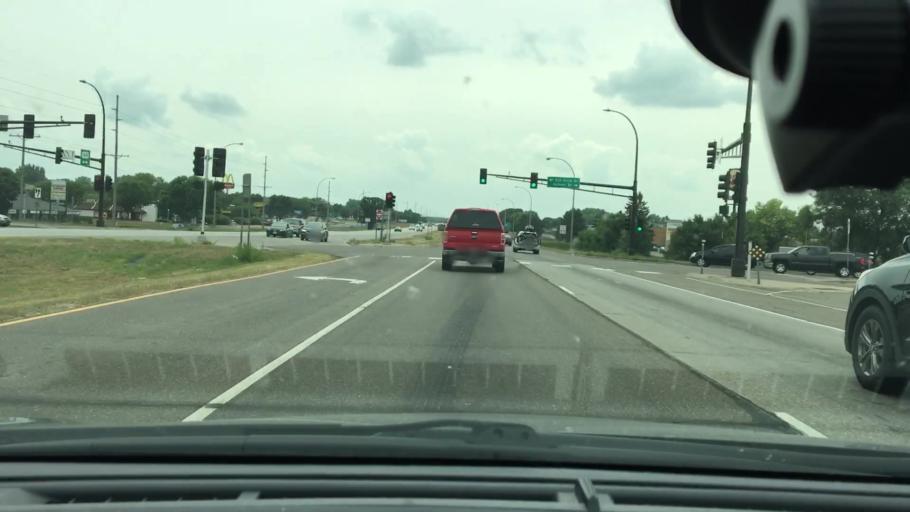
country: US
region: Minnesota
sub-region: Sherburne County
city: Elk River
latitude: 45.3122
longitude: -93.5588
